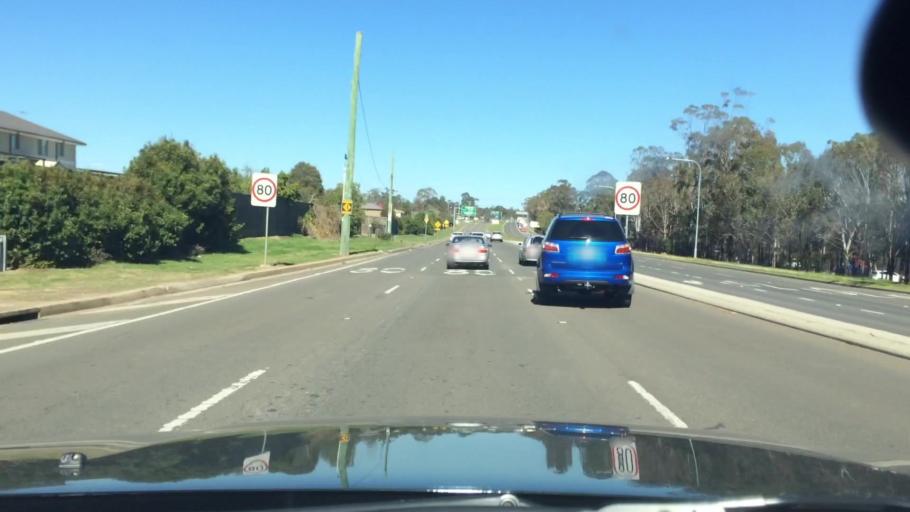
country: AU
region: New South Wales
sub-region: Campbelltown Municipality
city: Glenfield
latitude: -33.9598
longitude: 150.8850
